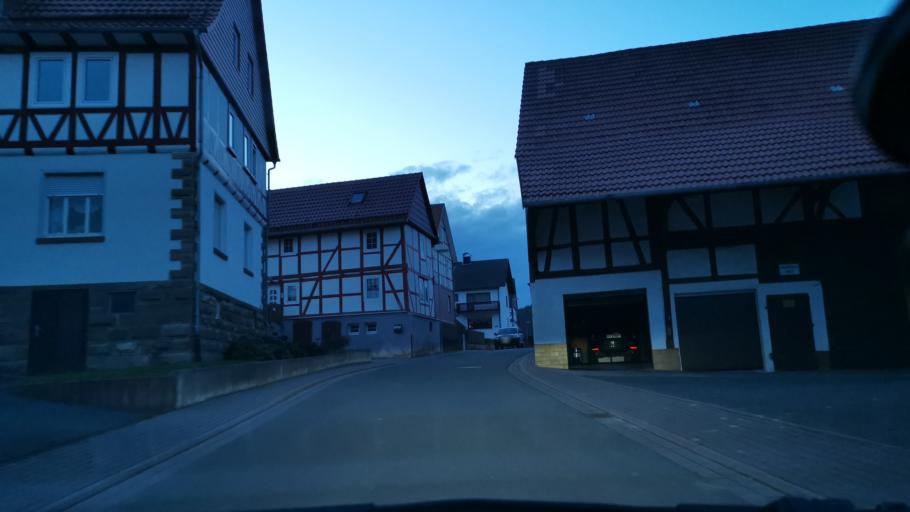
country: DE
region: Hesse
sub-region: Regierungsbezirk Kassel
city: Cornberg
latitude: 51.0539
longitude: 9.8492
